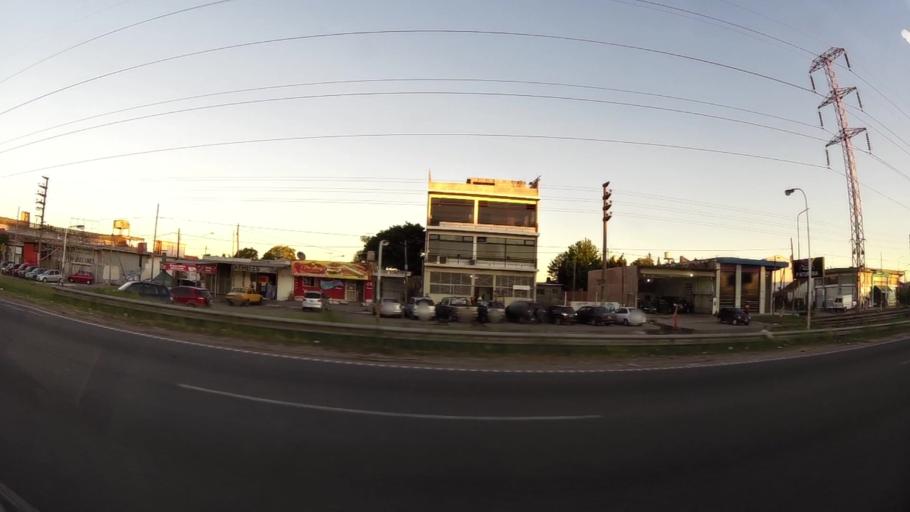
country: AR
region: Buenos Aires
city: Pontevedra
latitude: -34.7711
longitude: -58.6201
